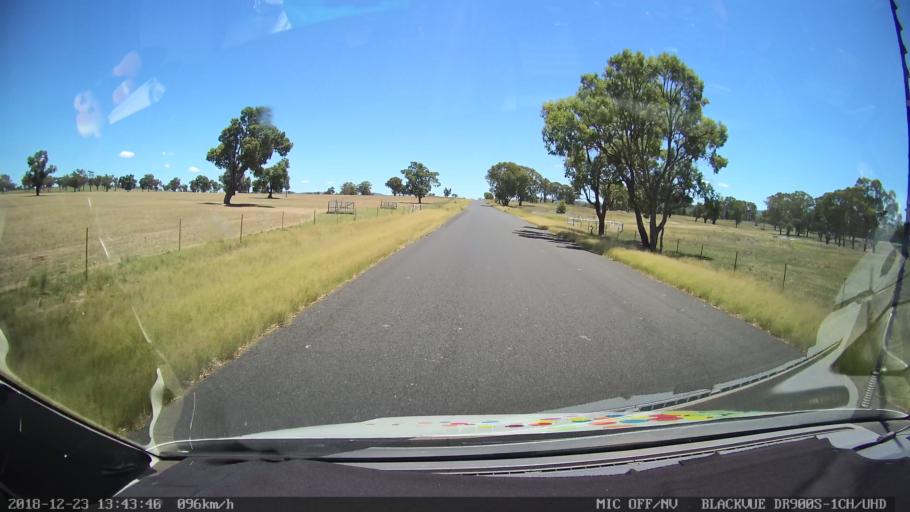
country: AU
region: New South Wales
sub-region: Tamworth Municipality
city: Manilla
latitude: -30.4877
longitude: 151.1466
